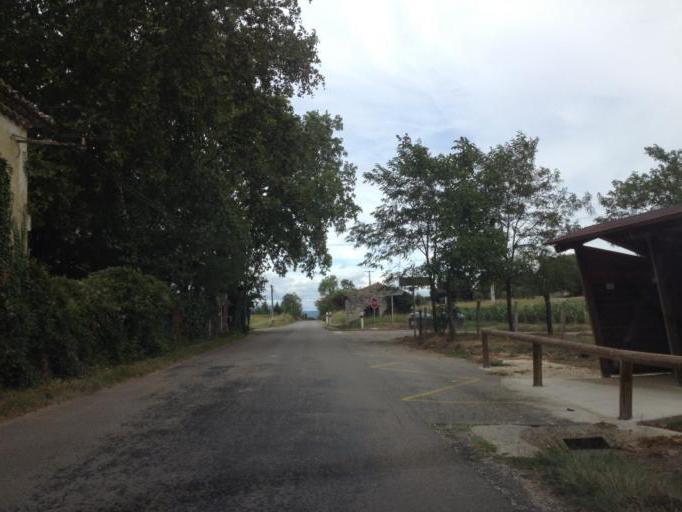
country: FR
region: Rhone-Alpes
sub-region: Departement de la Drome
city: Allan
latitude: 44.4837
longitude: 4.7966
